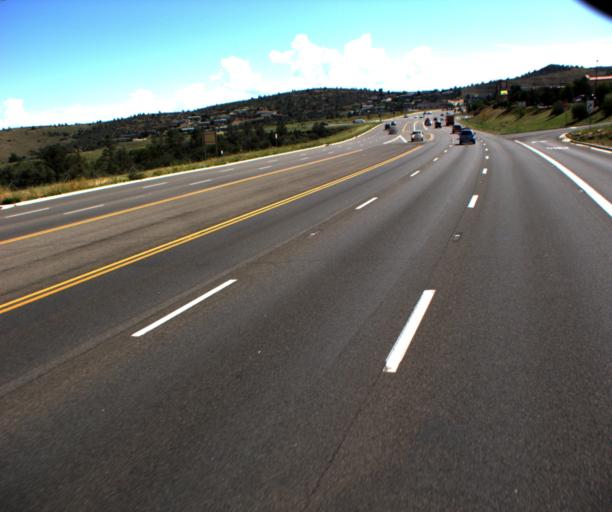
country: US
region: Arizona
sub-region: Yavapai County
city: Prescott
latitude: 34.5502
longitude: -112.4356
